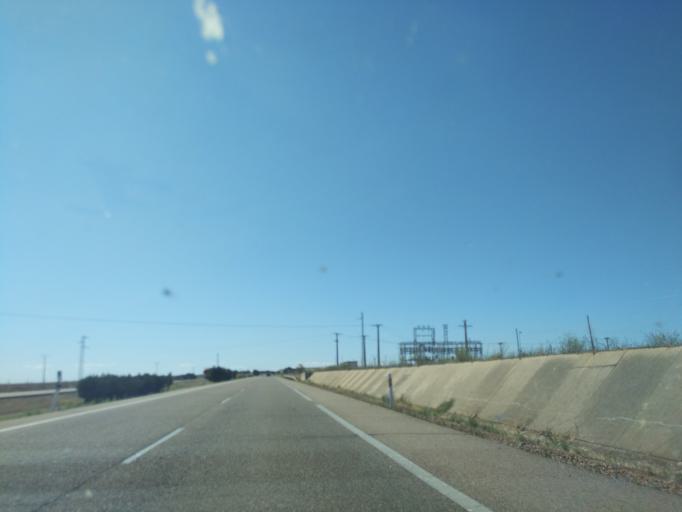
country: ES
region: Castille and Leon
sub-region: Provincia de Zamora
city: Villalpando
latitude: 41.8738
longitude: -5.4430
